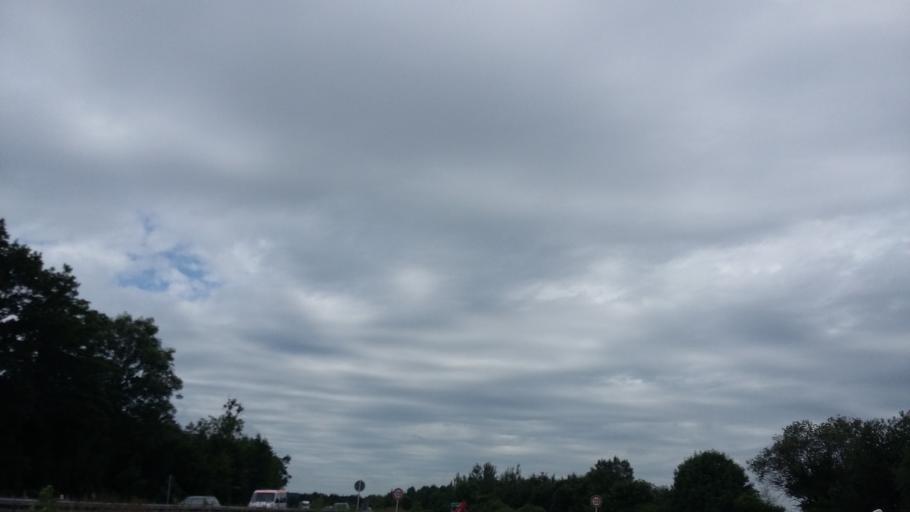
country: DE
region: Bavaria
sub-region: Upper Bavaria
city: Gilching
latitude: 48.0942
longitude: 11.2750
